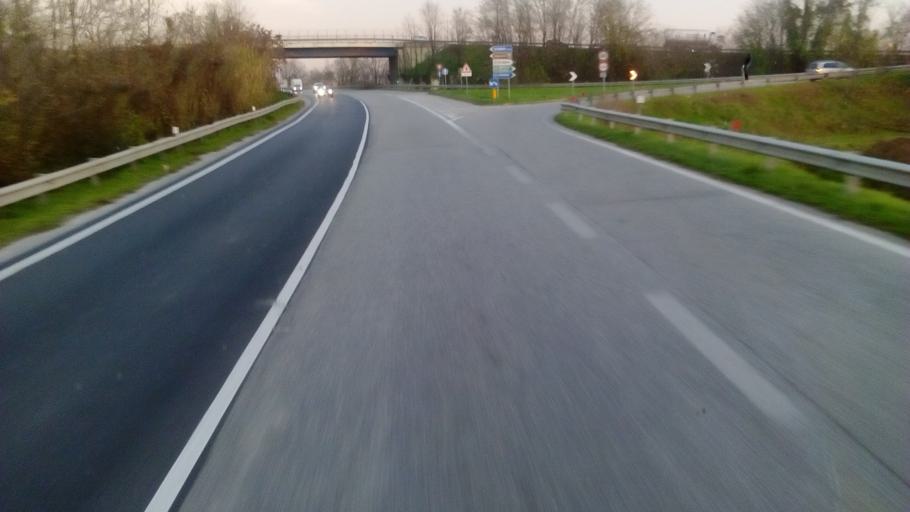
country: IT
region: Lombardy
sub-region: Provincia di Brescia
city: Orzinuovi
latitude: 45.4142
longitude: 9.9252
